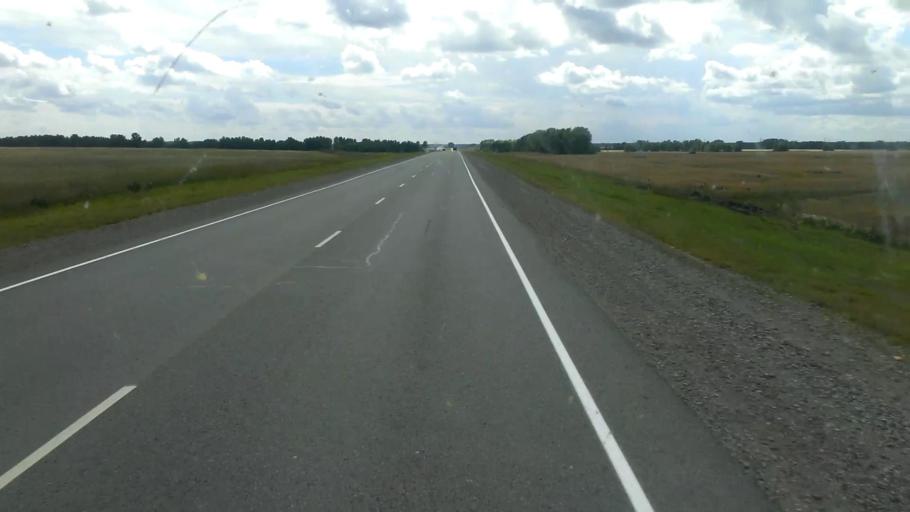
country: RU
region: Altai Krai
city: Troitskoye
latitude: 52.8975
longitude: 84.8338
